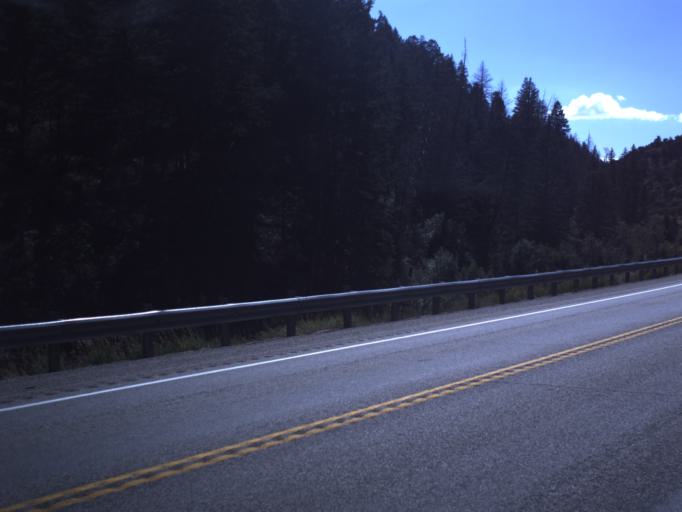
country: US
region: Utah
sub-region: Carbon County
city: Helper
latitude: 40.1967
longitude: -110.9260
